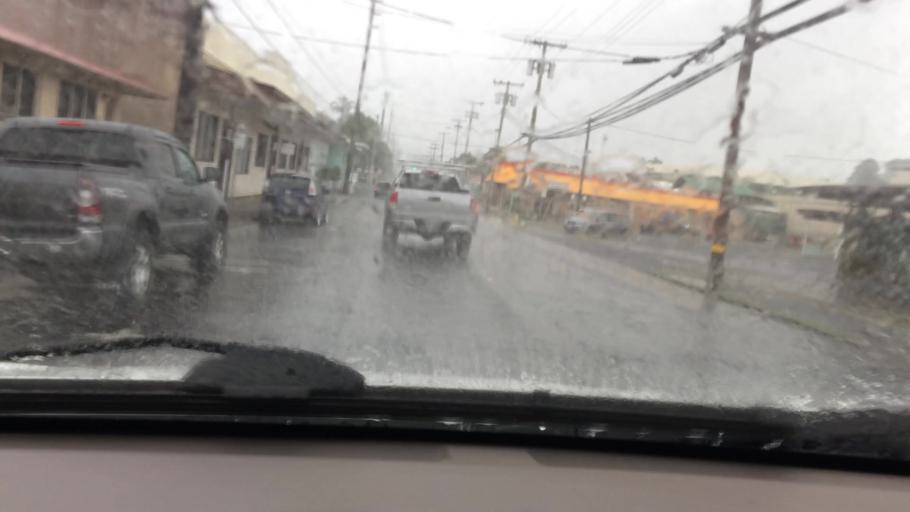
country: US
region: Hawaii
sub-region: Hawaii County
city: Hilo
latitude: 19.7226
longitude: -155.0874
